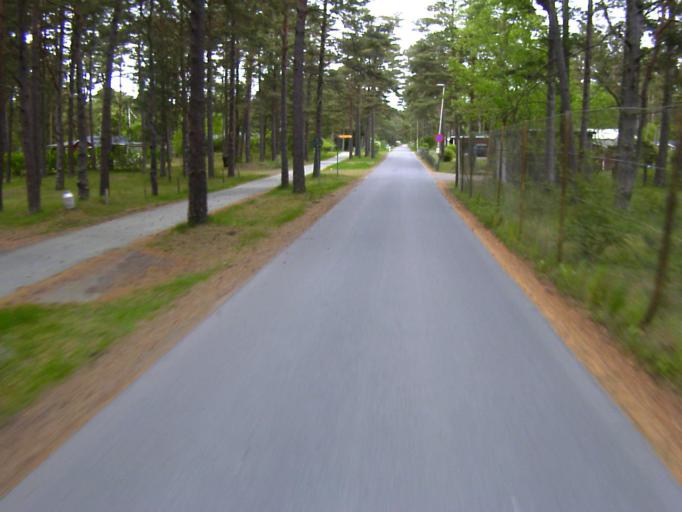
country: SE
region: Skane
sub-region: Kristianstads Kommun
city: Ahus
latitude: 55.9450
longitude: 14.3214
